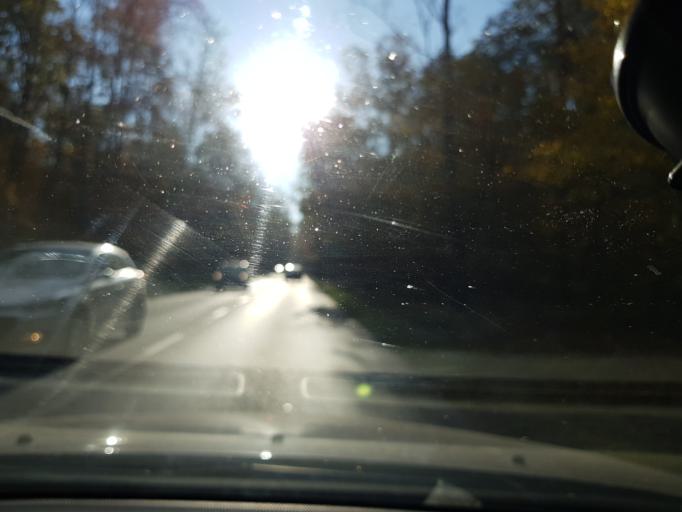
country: PL
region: Masovian Voivodeship
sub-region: Powiat warszawski zachodni
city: Babice
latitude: 52.2675
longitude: 20.8782
